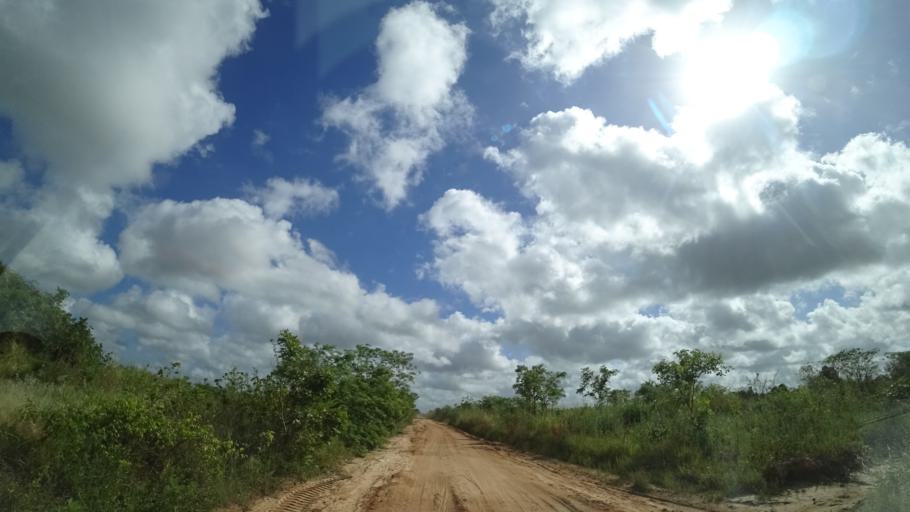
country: MZ
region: Sofala
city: Dondo
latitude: -19.4214
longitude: 34.7113
